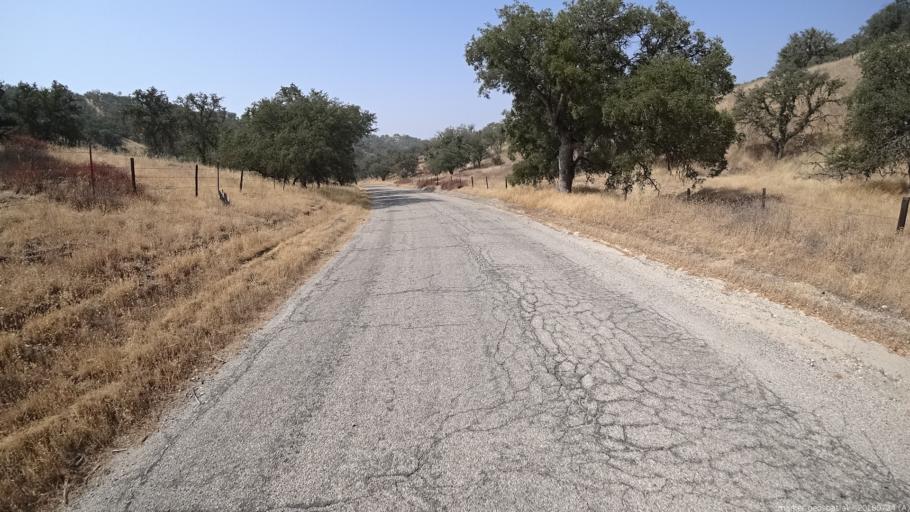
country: US
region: California
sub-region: San Luis Obispo County
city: San Miguel
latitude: 35.8818
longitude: -120.6805
